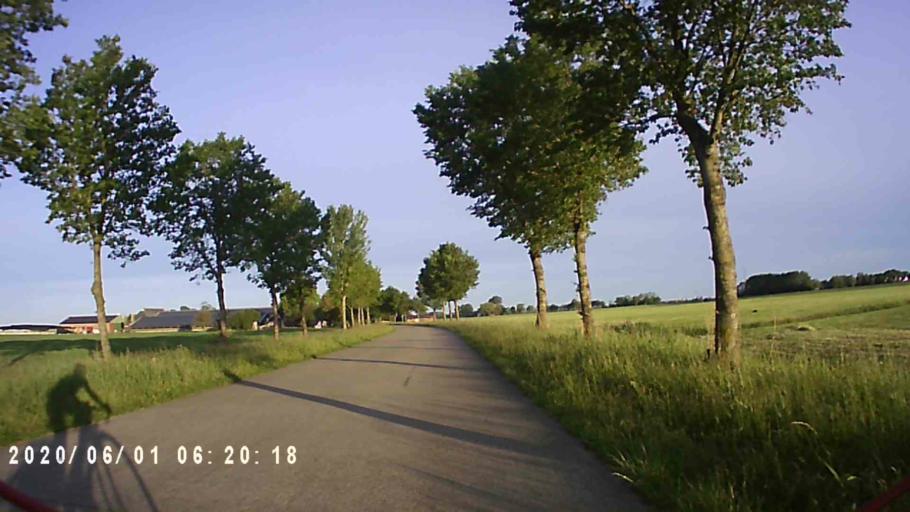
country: NL
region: Groningen
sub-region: Gemeente Grootegast
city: Grootegast
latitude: 53.2661
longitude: 6.2365
